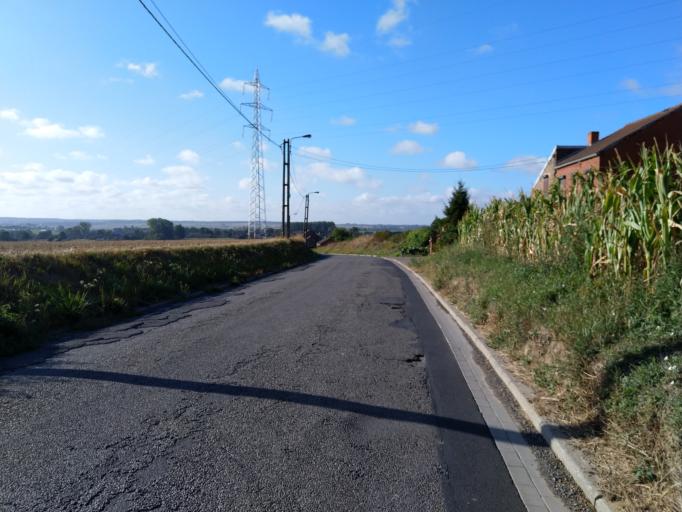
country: BE
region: Wallonia
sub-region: Province du Hainaut
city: Estinnes-au-Val
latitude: 50.4408
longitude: 4.0986
